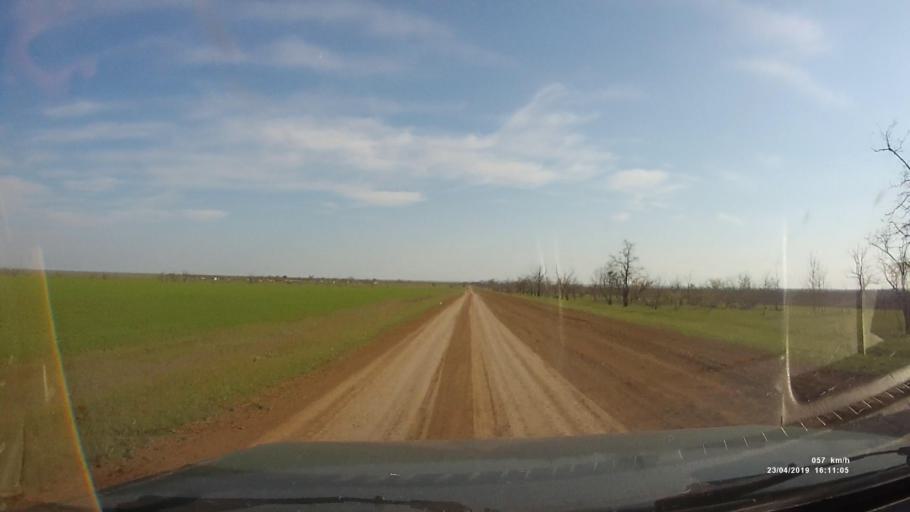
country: RU
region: Rostov
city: Remontnoye
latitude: 46.4770
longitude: 43.1231
